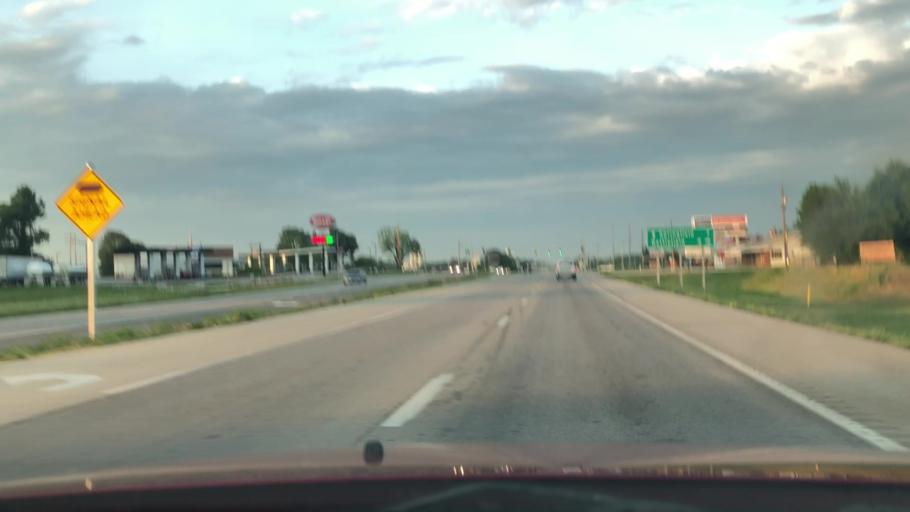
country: US
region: Missouri
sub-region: Greene County
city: Republic
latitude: 37.1444
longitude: -93.4314
